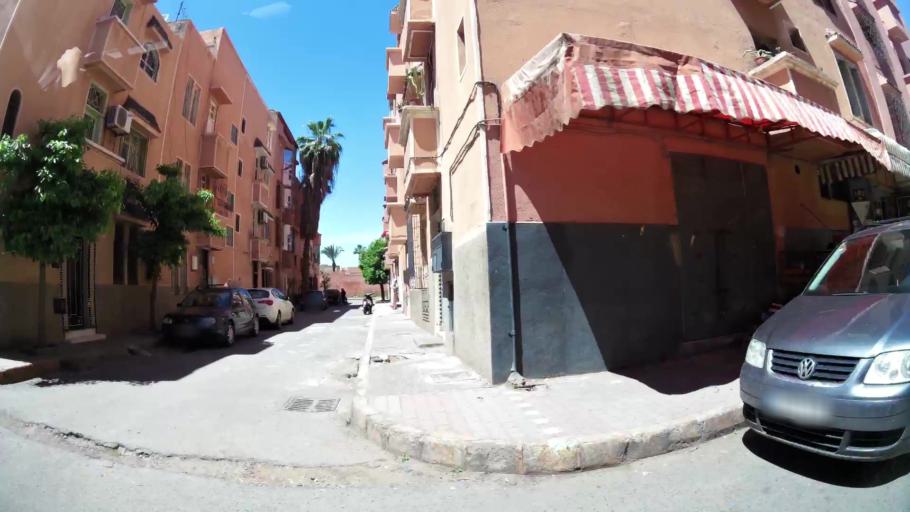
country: MA
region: Marrakech-Tensift-Al Haouz
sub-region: Marrakech
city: Marrakesh
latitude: 31.6288
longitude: -8.0526
